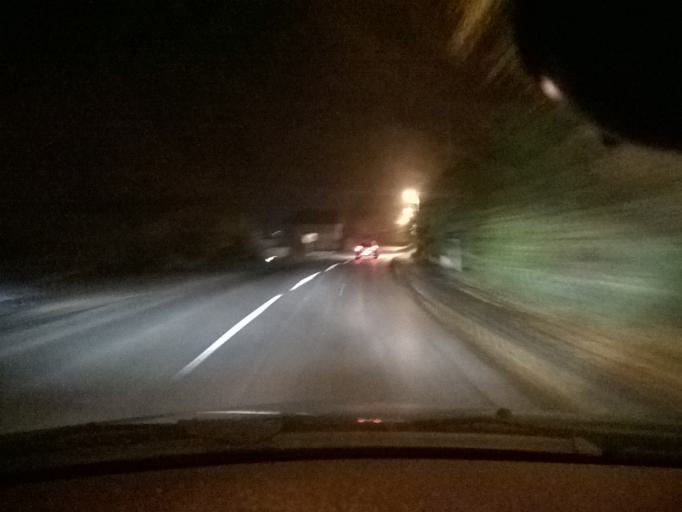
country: HR
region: Krapinsko-Zagorska
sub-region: Grad Krapina
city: Krapina
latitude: 46.1425
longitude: 15.8811
